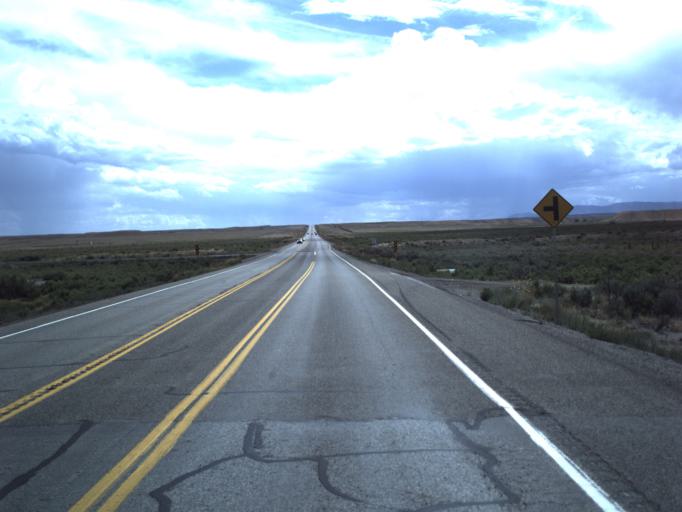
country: US
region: Utah
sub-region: Carbon County
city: Price
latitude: 39.5180
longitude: -110.8281
